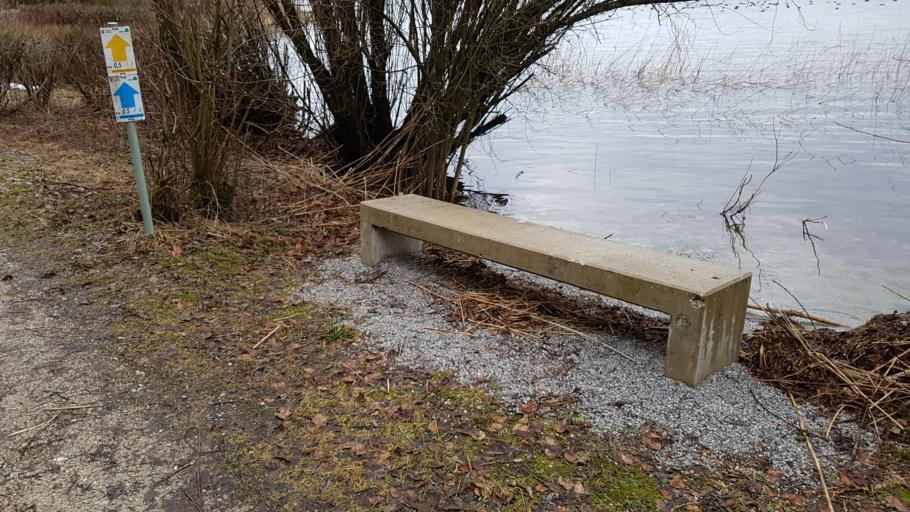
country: AT
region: Salzburg
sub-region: Politischer Bezirk Salzburg-Umgebung
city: Henndorf am Wallersee
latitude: 47.9076
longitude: 13.1774
